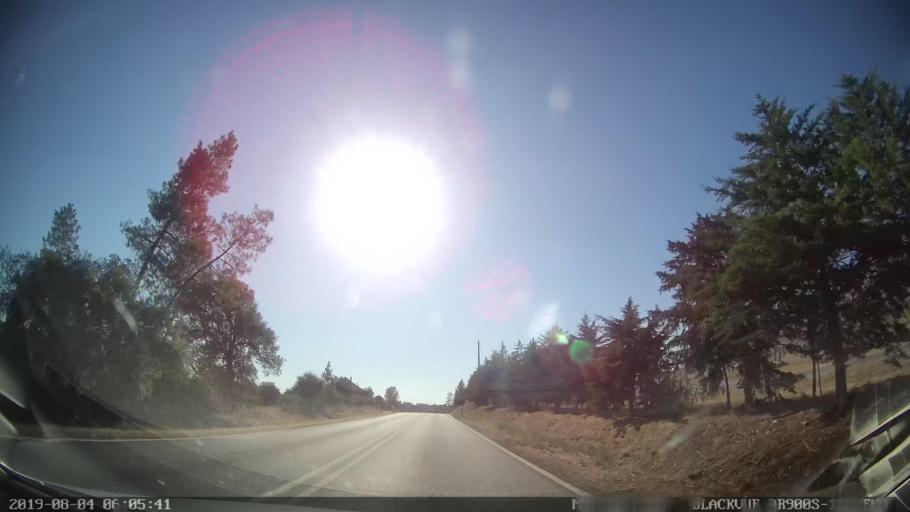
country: PT
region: Santarem
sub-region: Abrantes
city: Alferrarede
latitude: 39.4758
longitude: -8.0784
